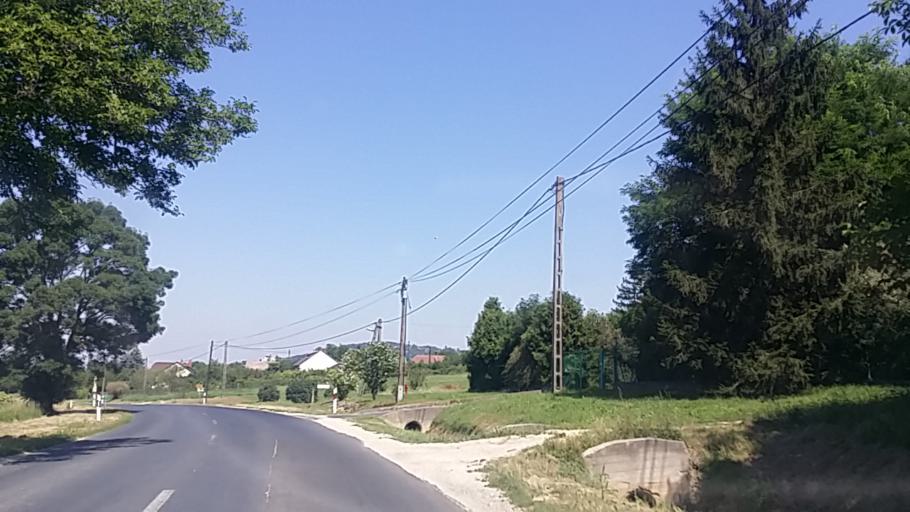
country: HU
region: Zala
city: Cserszegtomaj
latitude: 46.8070
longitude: 17.2063
